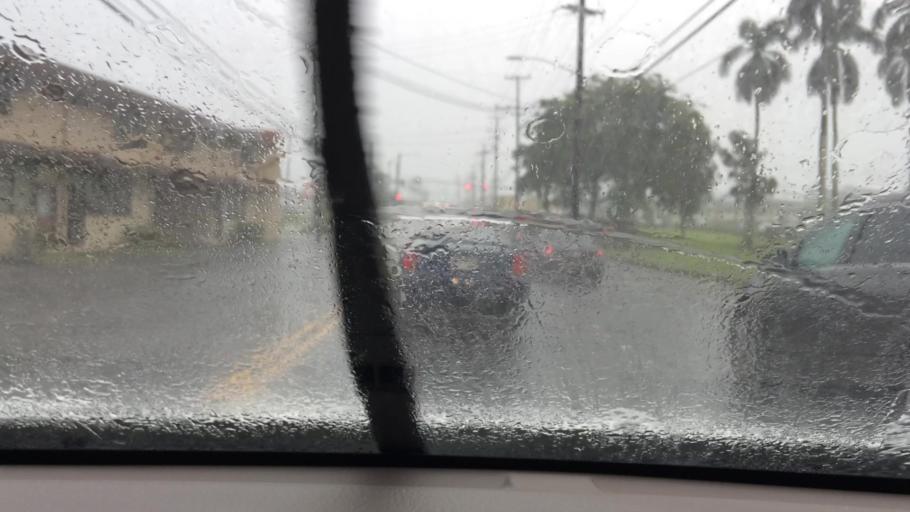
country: US
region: Hawaii
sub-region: Hawaii County
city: Hilo
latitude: 19.7149
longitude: -155.0778
